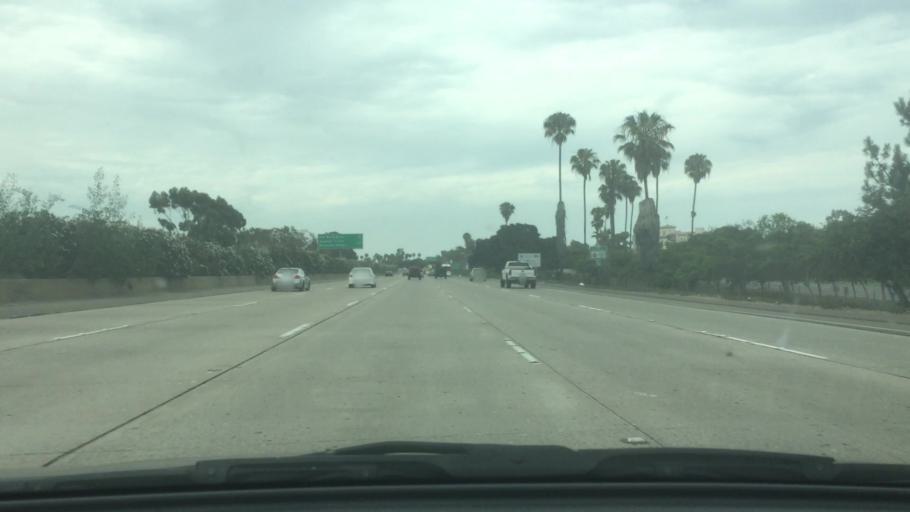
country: US
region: California
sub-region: San Diego County
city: San Diego
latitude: 32.7843
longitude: -117.2078
